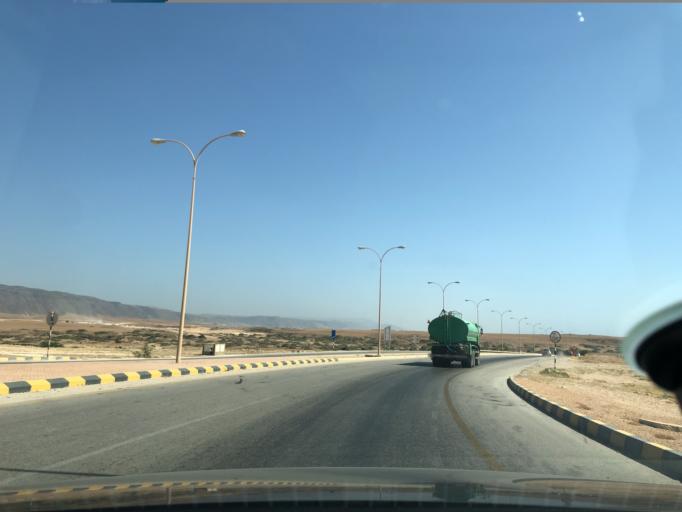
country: OM
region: Zufar
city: Salalah
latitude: 17.0505
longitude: 54.3259
